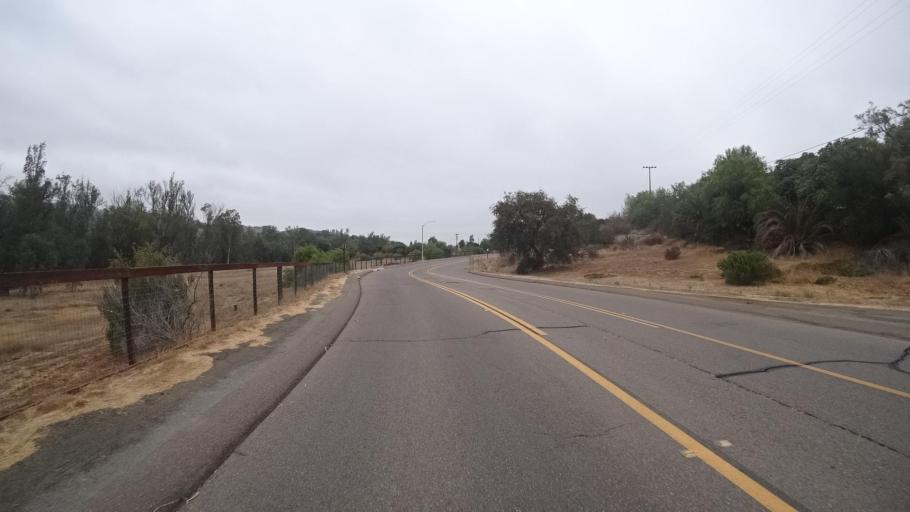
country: US
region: California
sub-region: San Diego County
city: Escondido
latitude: 33.1113
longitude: -117.1276
